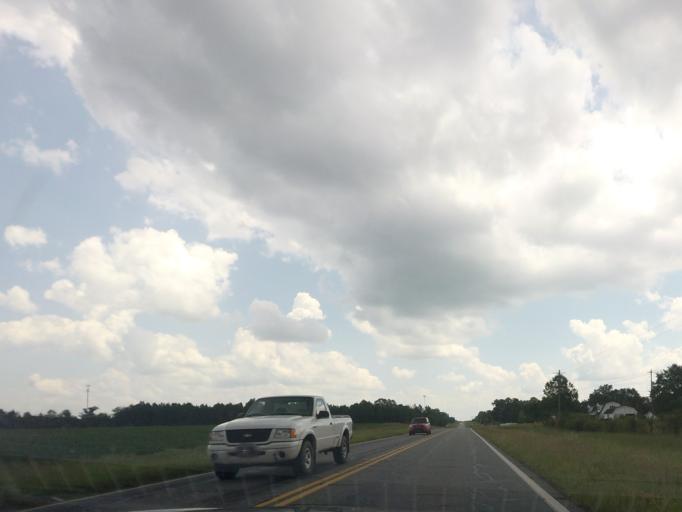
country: US
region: Georgia
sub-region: Bleckley County
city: Cochran
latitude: 32.4141
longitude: -83.3500
